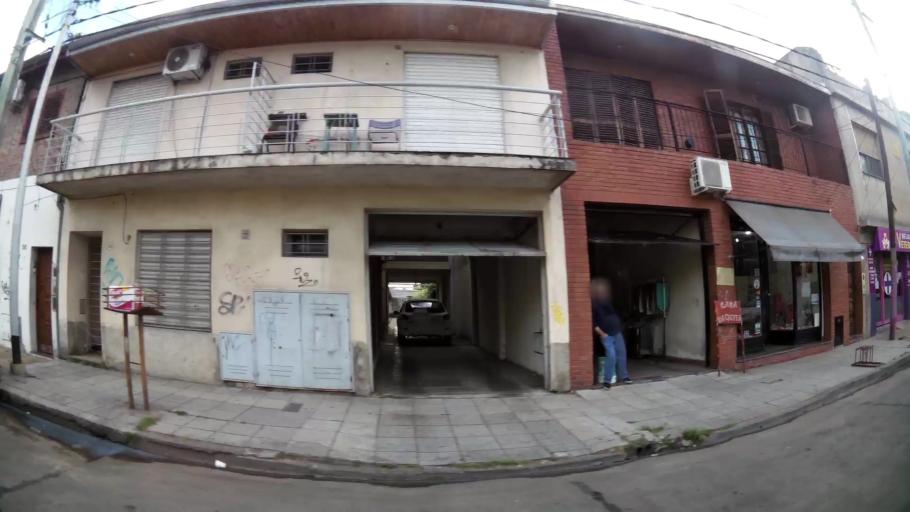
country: AR
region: Buenos Aires
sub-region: Partido de Avellaneda
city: Avellaneda
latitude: -34.6831
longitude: -58.3483
